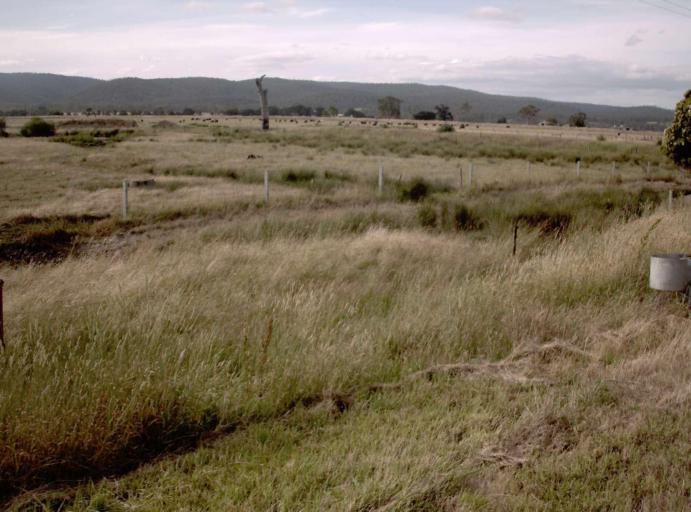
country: AU
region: Victoria
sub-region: Wellington
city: Heyfield
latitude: -38.0161
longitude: 146.6709
